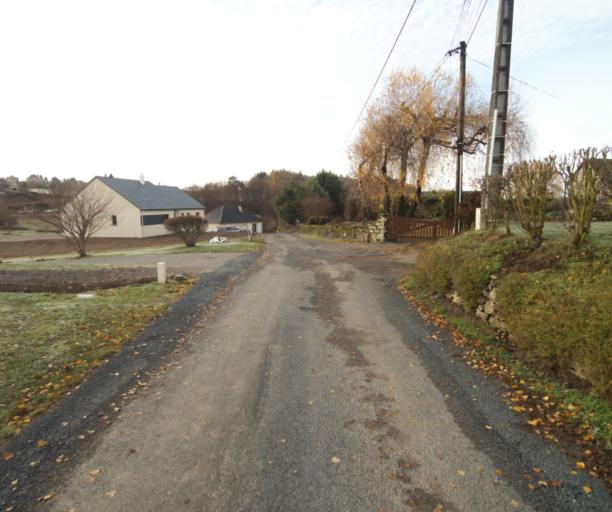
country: FR
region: Limousin
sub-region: Departement de la Correze
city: Cornil
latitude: 45.2133
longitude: 1.7113
